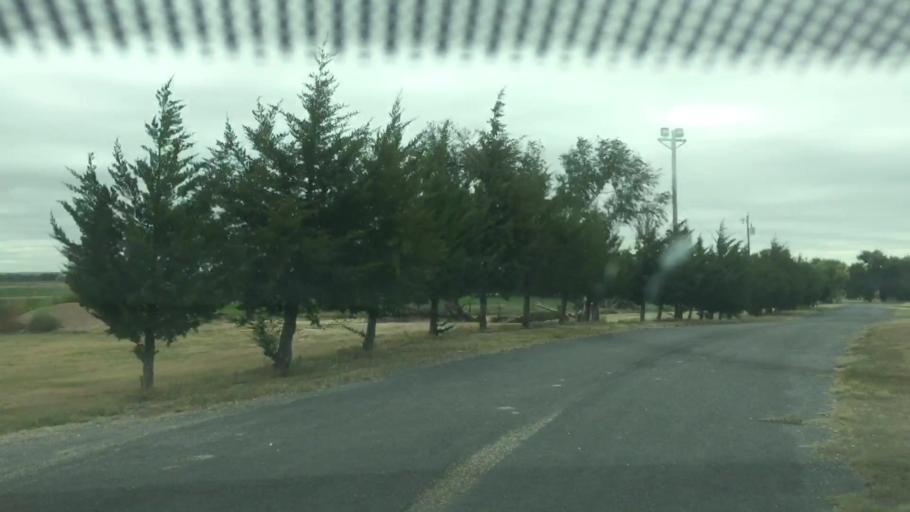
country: US
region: Kansas
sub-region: Hamilton County
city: Syracuse
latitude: 38.0581
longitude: -102.1089
